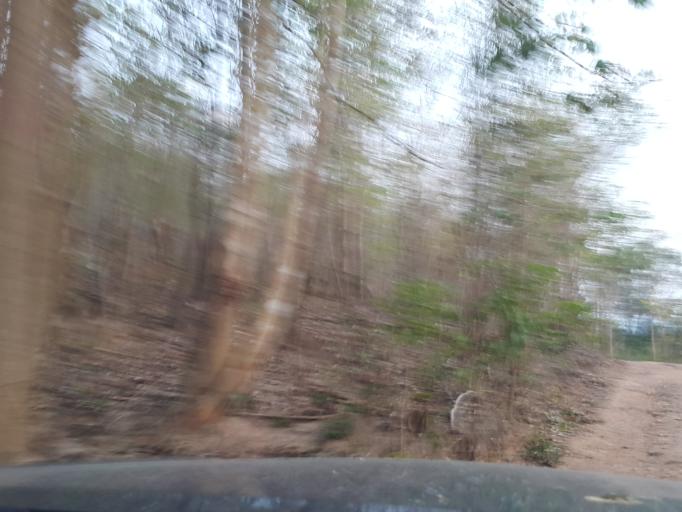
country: TH
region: Lamphun
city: Thung Hua Chang
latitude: 17.9012
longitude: 99.0817
